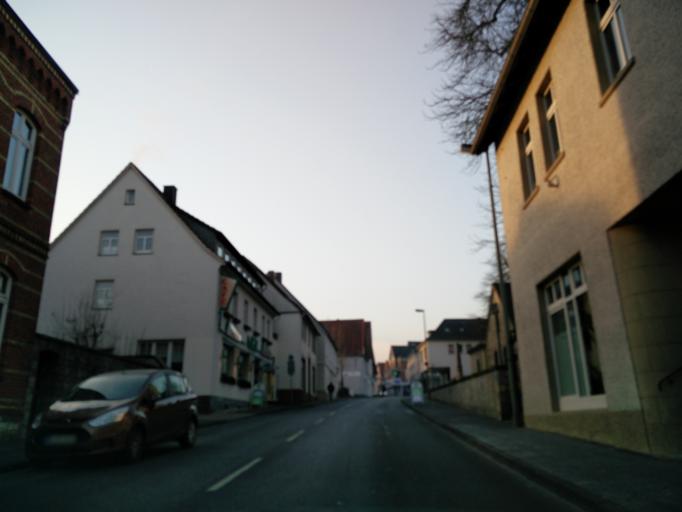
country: DE
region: North Rhine-Westphalia
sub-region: Regierungsbezirk Detmold
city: Buren
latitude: 51.5536
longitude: 8.5600
